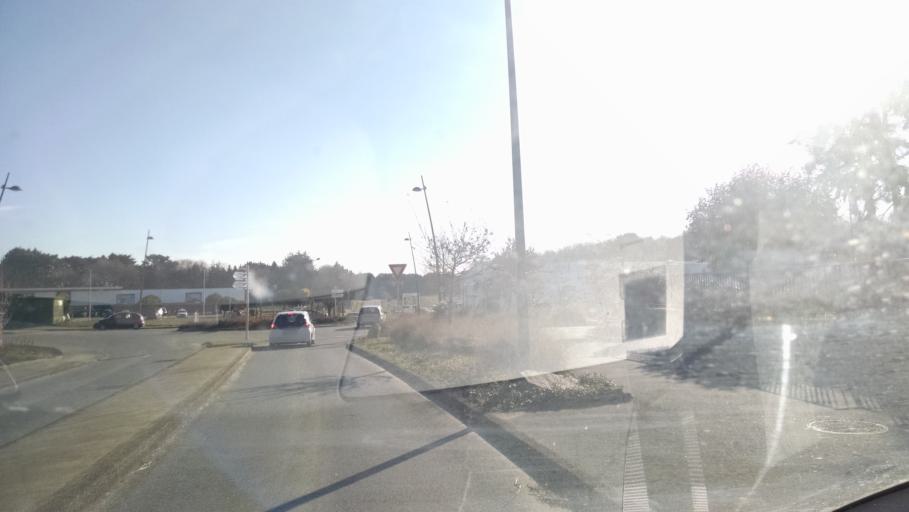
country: FR
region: Brittany
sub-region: Departement du Morbihan
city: Gestel
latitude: 47.7998
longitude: -3.4779
